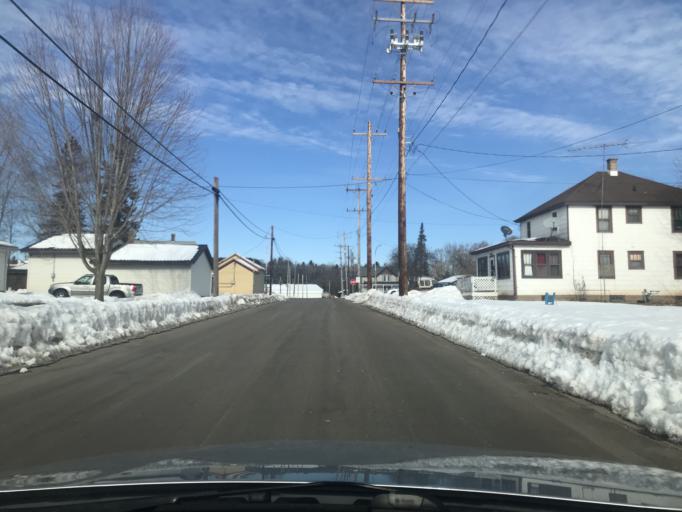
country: US
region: Wisconsin
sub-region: Oconto County
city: Gillett
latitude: 44.8900
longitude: -88.3024
